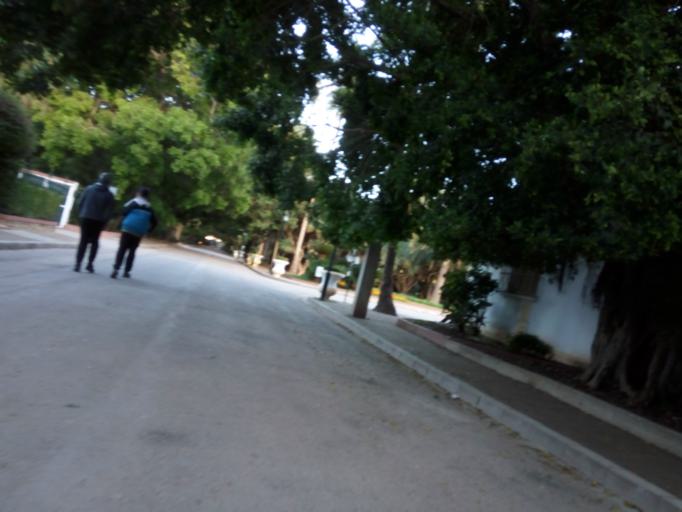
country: DZ
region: Alger
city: Algiers
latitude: 36.7505
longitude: 3.0762
